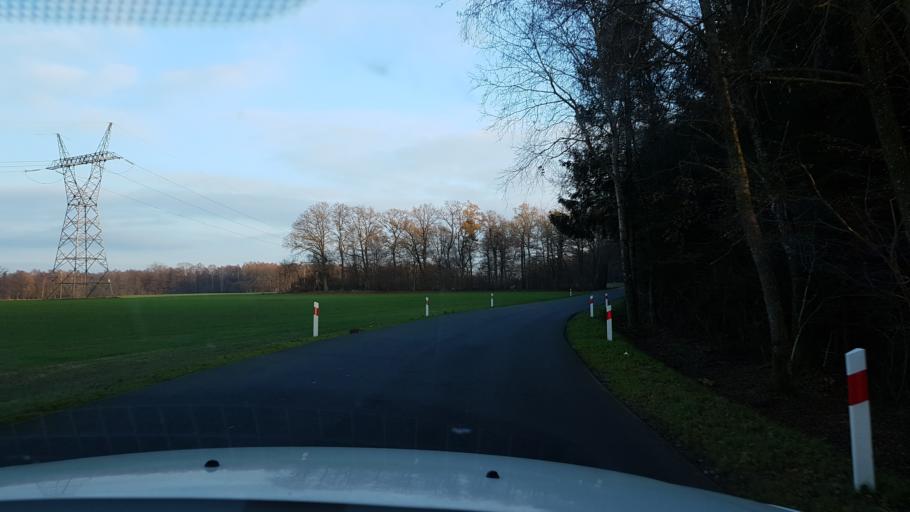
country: PL
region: West Pomeranian Voivodeship
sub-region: Koszalin
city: Koszalin
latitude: 54.1216
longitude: 16.0964
